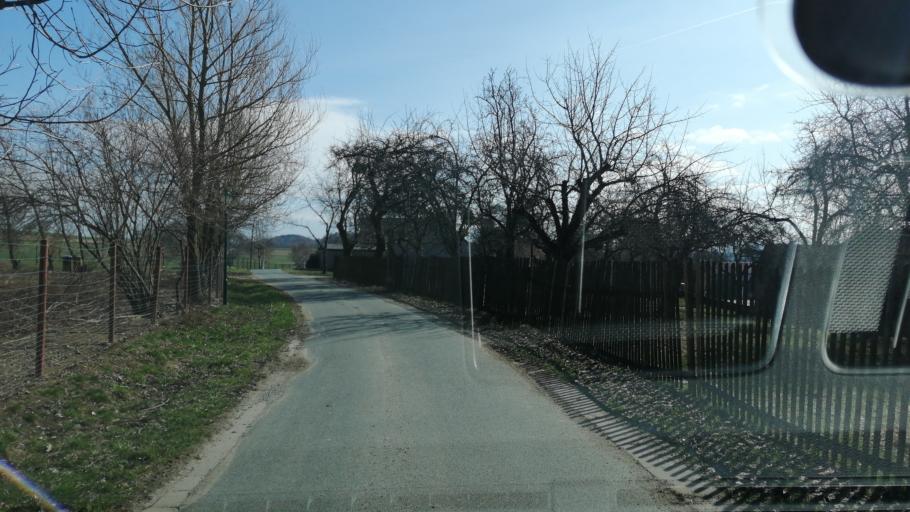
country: DE
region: Saxony
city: Schonbach
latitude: 51.0688
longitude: 14.5536
